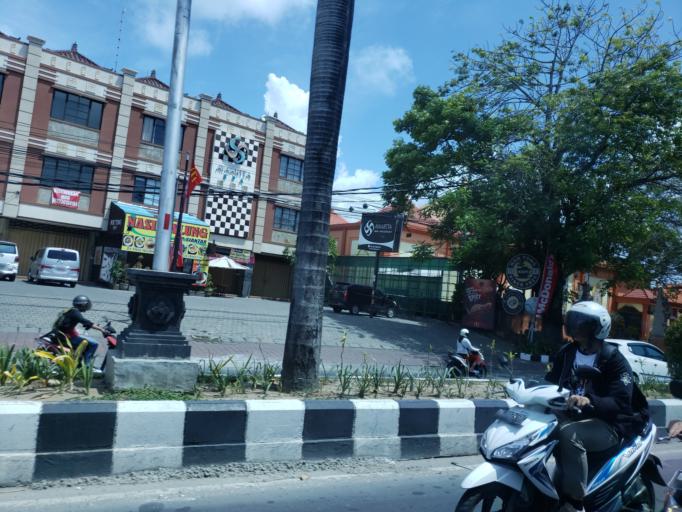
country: ID
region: Bali
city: Jabajero
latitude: -8.7310
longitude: 115.1787
